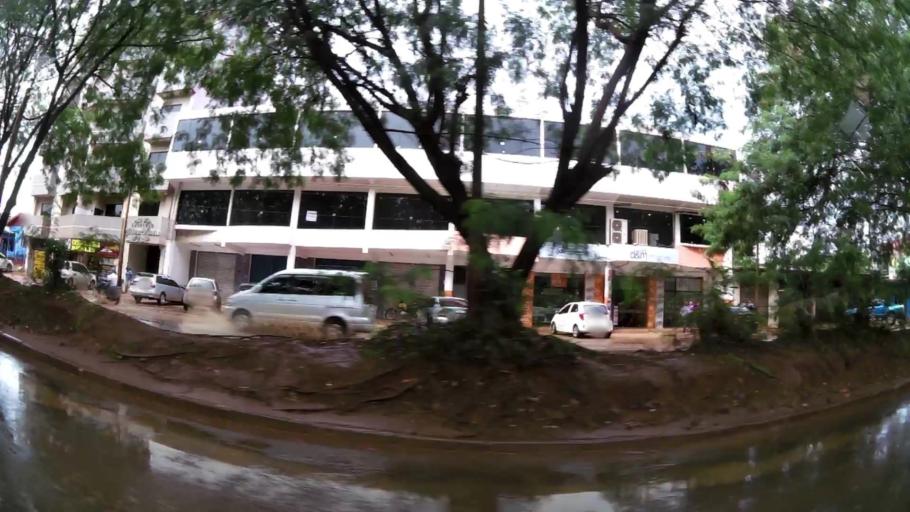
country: PY
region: Alto Parana
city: Presidente Franco
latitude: -25.5147
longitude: -54.6470
